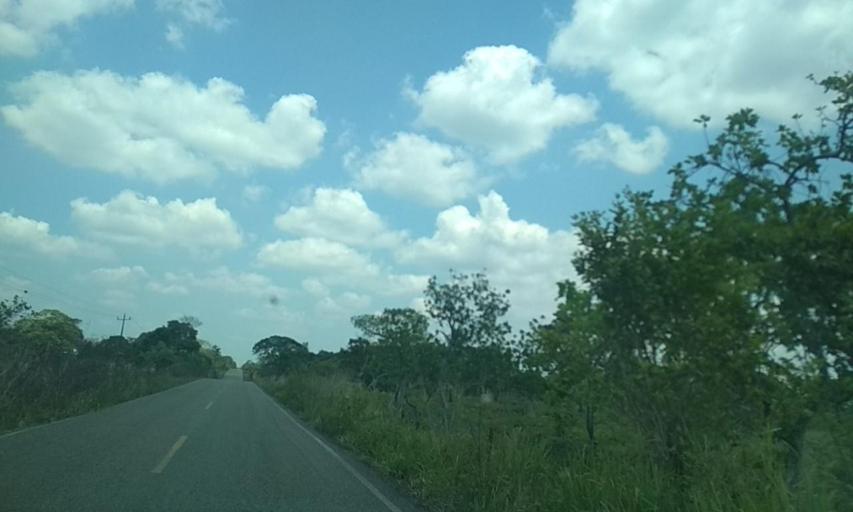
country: MX
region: Tabasco
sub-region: Huimanguillo
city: Huapacal 1ra. Seccion
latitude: 17.7543
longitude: -93.7527
